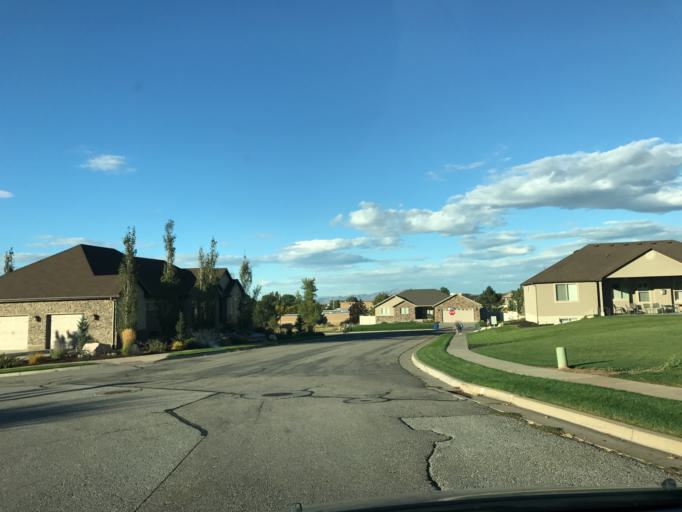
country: US
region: Utah
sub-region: Davis County
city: South Weber
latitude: 41.1060
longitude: -111.9258
